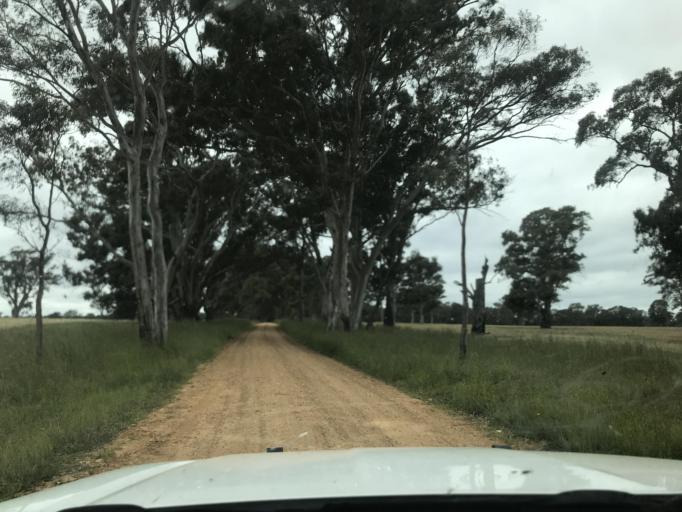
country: AU
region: South Australia
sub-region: Wattle Range
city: Penola
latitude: -37.2705
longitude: 140.9725
